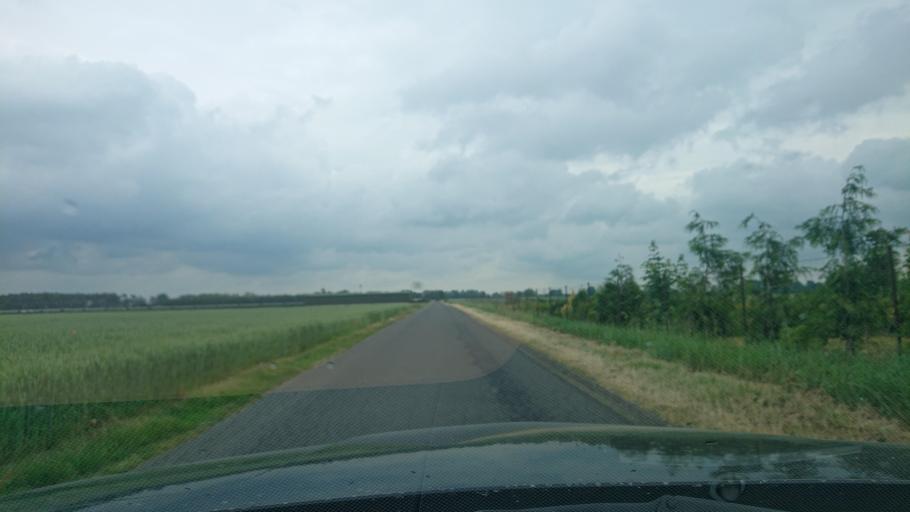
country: PL
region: Greater Poland Voivodeship
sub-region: Powiat gnieznienski
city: Czerniejewo
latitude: 52.4787
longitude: 17.5240
